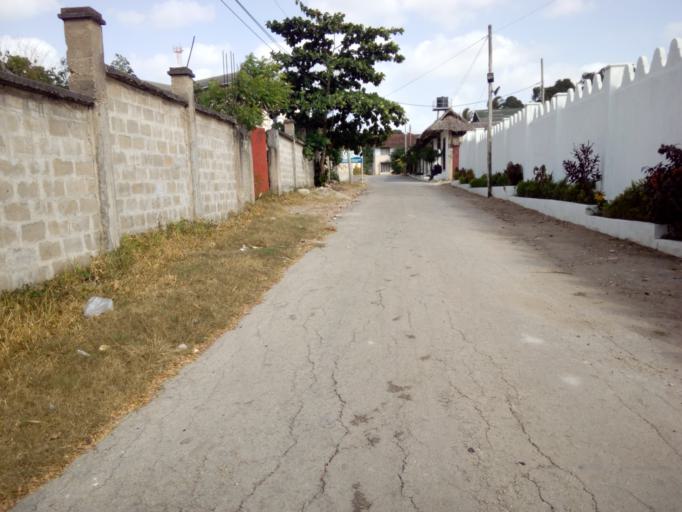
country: TZ
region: Zanzibar Urban/West
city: Zanzibar
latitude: -6.1807
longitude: 39.2031
